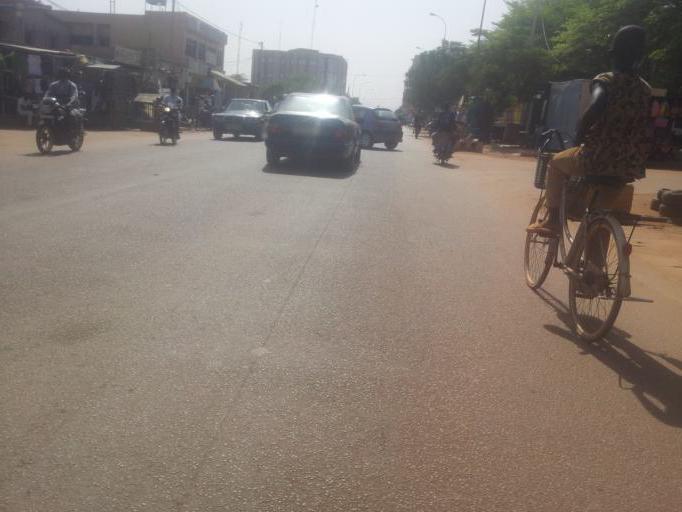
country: BF
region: Centre
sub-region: Kadiogo Province
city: Ouagadougou
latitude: 12.3773
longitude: -1.5337
